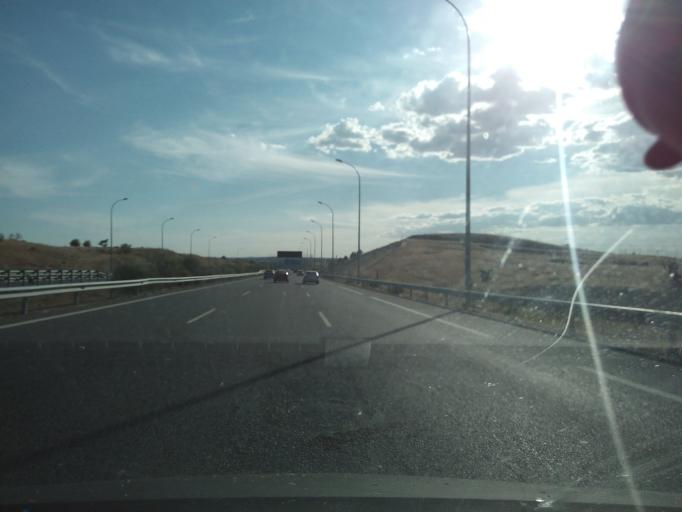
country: ES
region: Madrid
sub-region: Provincia de Madrid
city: Villa de Vallecas
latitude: 40.3395
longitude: -3.6072
